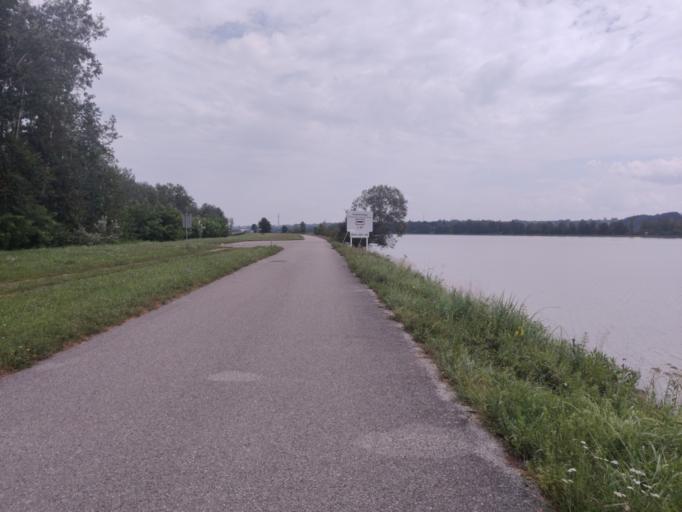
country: AT
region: Lower Austria
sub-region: Politischer Bezirk Amstetten
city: Strengberg
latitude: 48.1679
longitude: 14.6656
